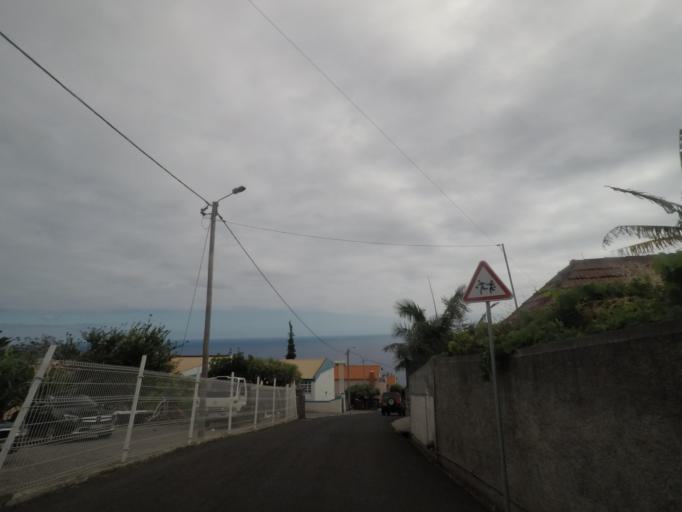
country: PT
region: Madeira
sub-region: Calheta
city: Arco da Calheta
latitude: 32.7128
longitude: -17.1484
